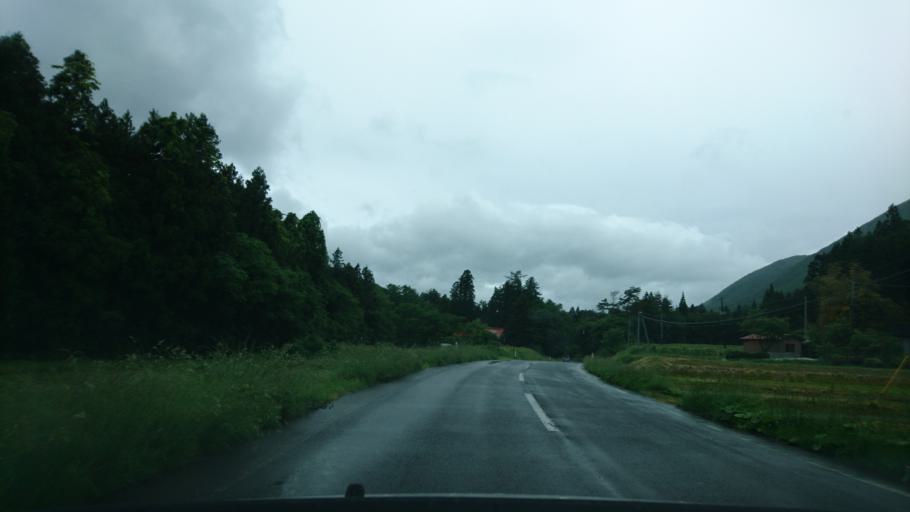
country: JP
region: Iwate
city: Ichinoseki
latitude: 38.9934
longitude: 140.9032
